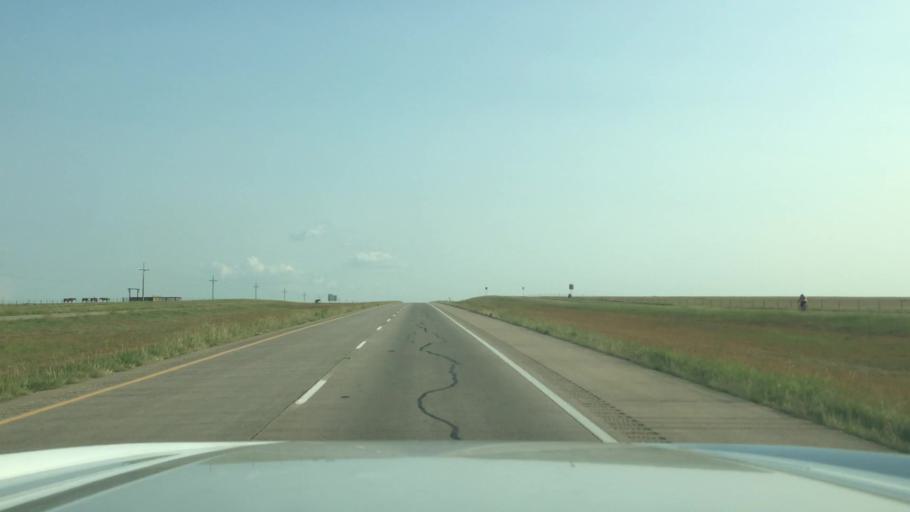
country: US
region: Texas
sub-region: Randall County
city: Canyon
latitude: 34.9237
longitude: -101.8487
